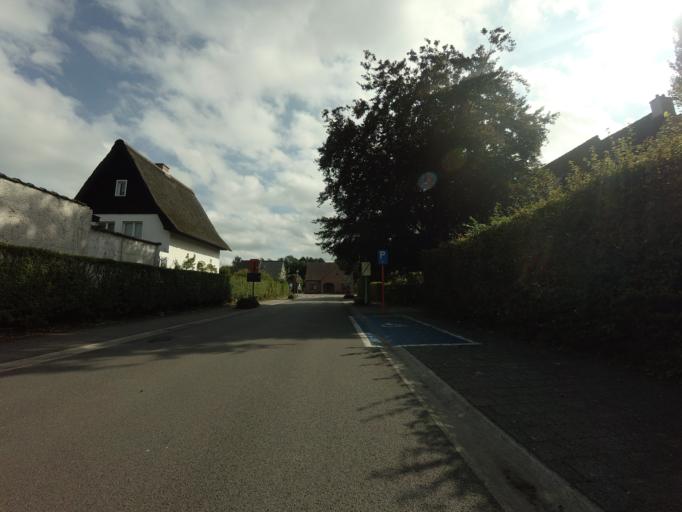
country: BE
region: Flanders
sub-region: Provincie Antwerpen
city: Boom
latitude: 51.1113
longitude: 4.3802
